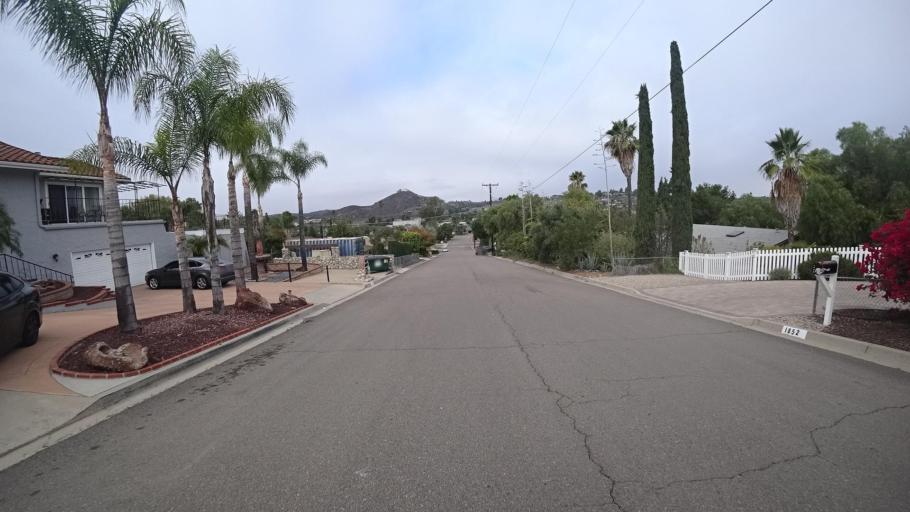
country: US
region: California
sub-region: San Diego County
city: Rancho San Diego
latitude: 32.7601
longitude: -116.9161
